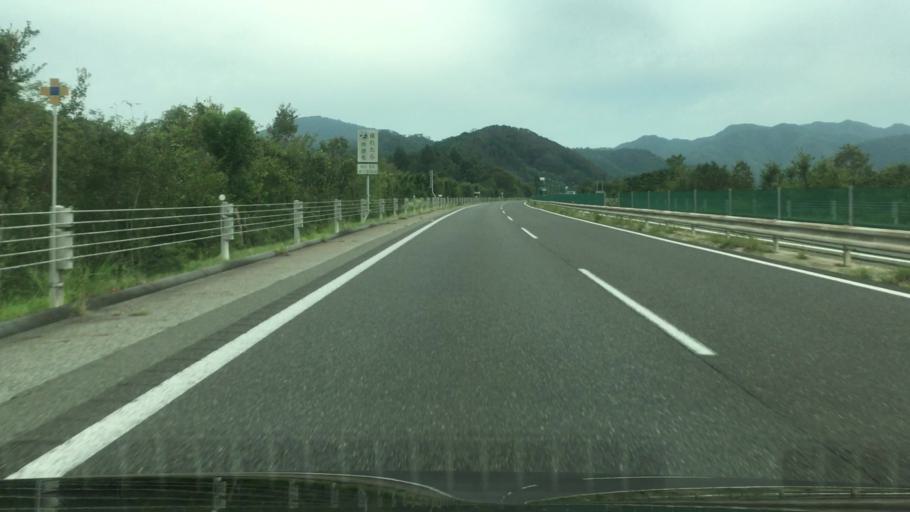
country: JP
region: Hyogo
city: Sasayama
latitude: 35.0830
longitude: 135.1677
